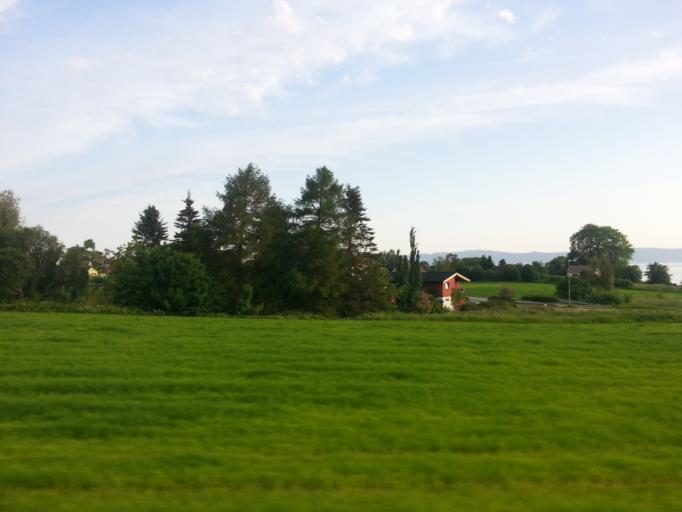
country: NO
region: Sor-Trondelag
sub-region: Malvik
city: Malvik
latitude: 63.4275
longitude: 10.5571
